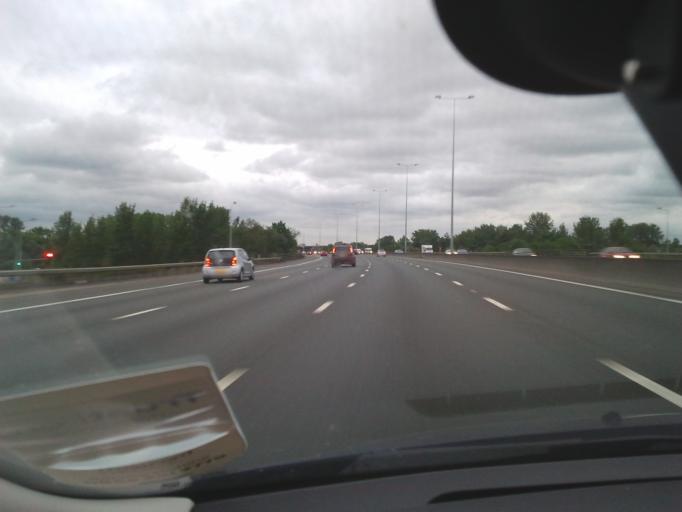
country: GB
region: England
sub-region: Surrey
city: Staines
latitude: 51.4459
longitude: -0.5279
